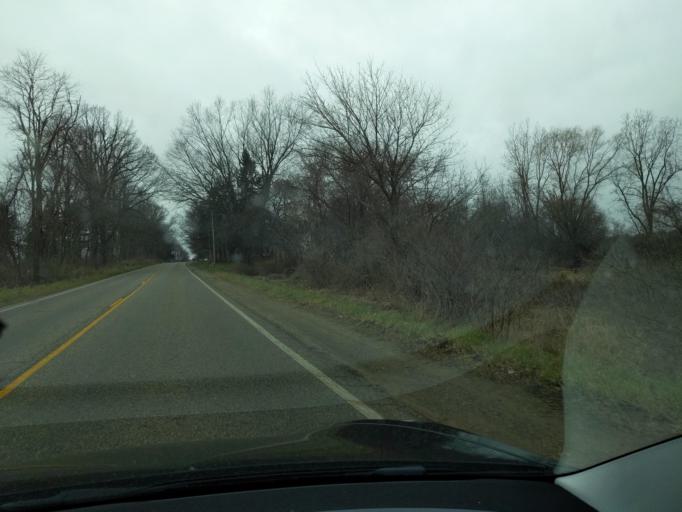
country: US
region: Michigan
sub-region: Jackson County
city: Spring Arbor
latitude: 42.2525
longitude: -84.5218
